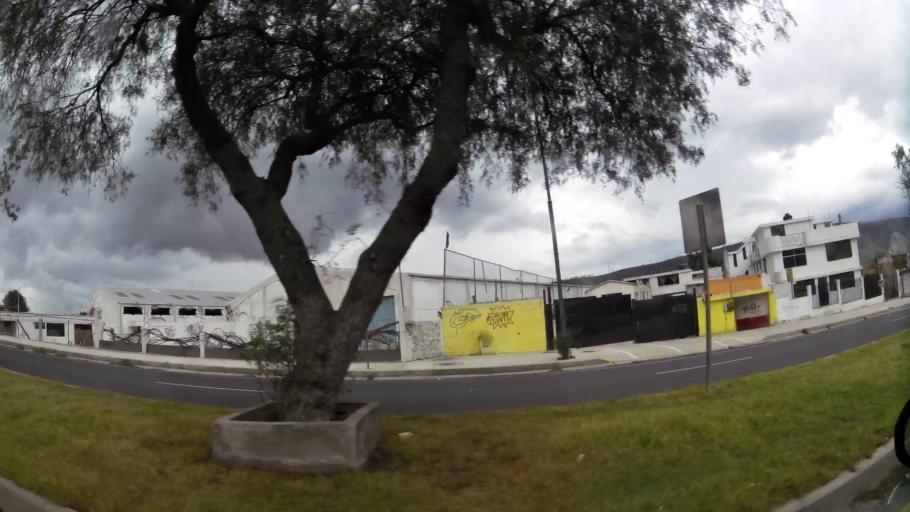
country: EC
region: Pichincha
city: Quito
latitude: -0.0068
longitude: -78.4530
